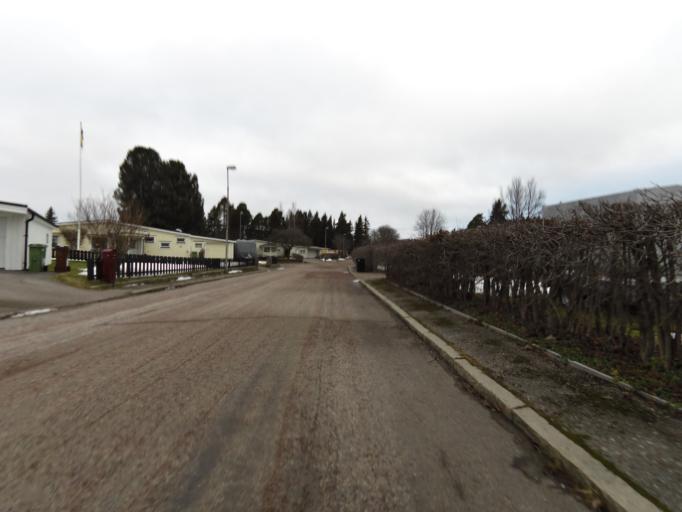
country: SE
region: Gaevleborg
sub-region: Gavle Kommun
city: Gavle
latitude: 60.6573
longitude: 17.1468
